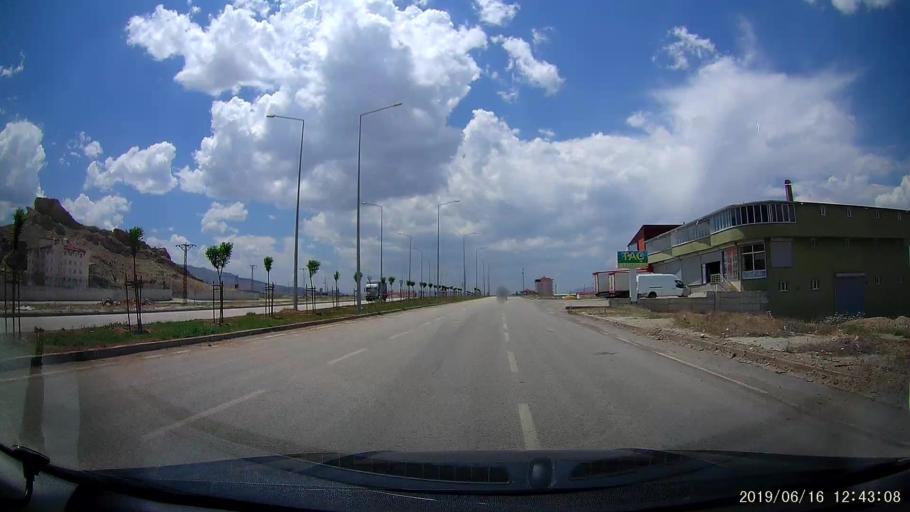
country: TR
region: Agri
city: Dogubayazit
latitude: 39.5585
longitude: 44.1218
